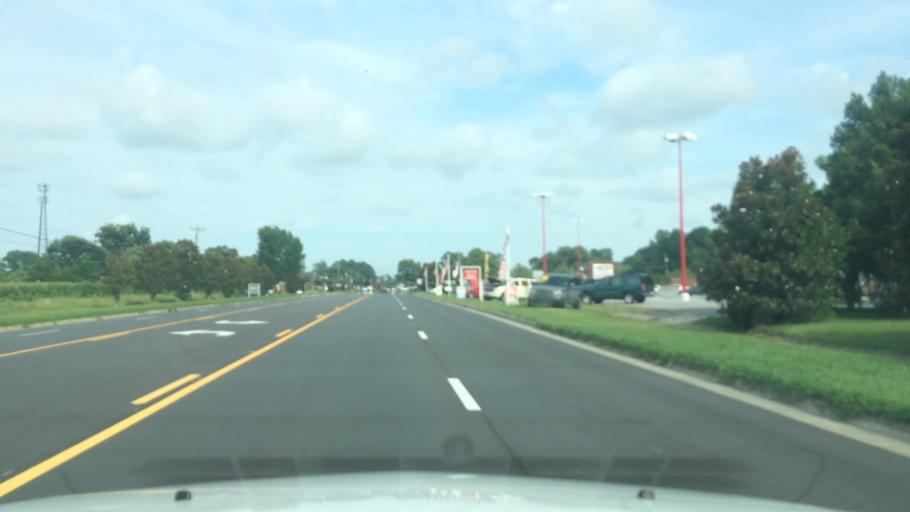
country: US
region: North Carolina
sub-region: Pitt County
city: Farmville
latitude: 35.5838
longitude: -77.5984
